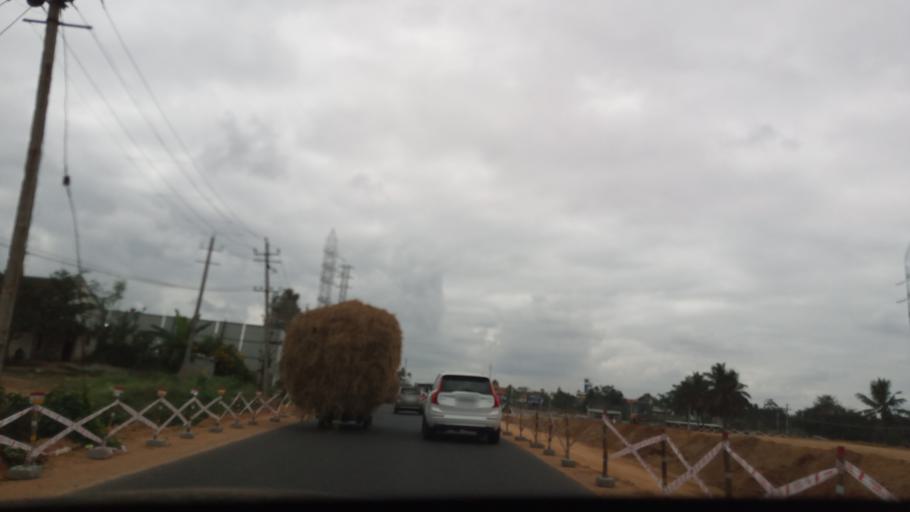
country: IN
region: Karnataka
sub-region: Mandya
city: Mandya
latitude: 12.4956
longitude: 76.8014
